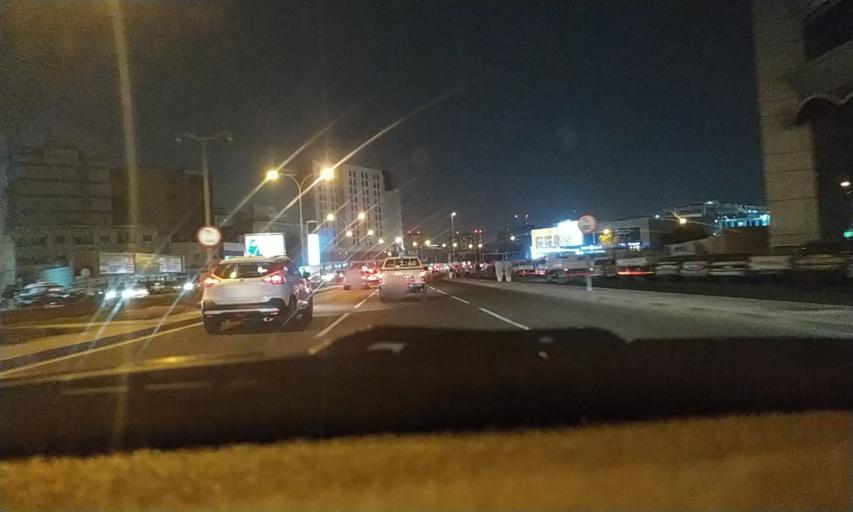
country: QA
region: Baladiyat ad Dawhah
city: Doha
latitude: 25.2775
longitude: 51.5375
